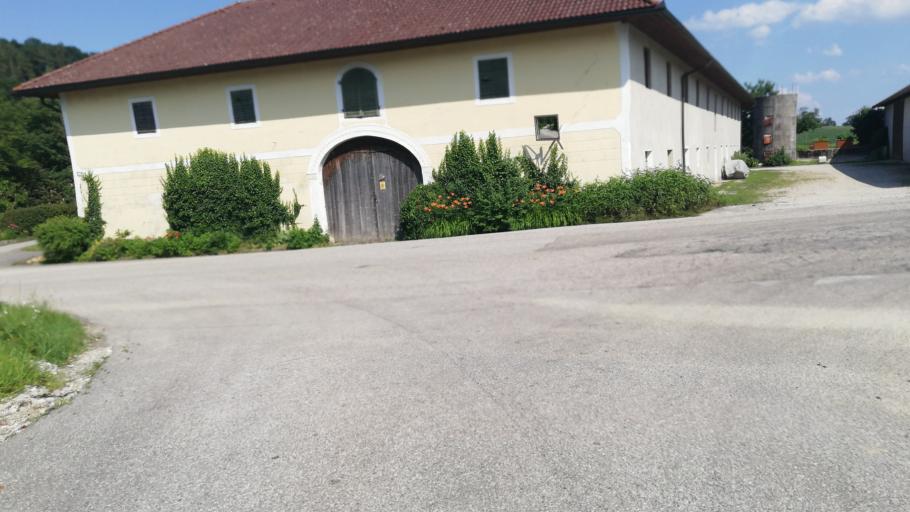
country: AT
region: Upper Austria
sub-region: Wels-Land
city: Gunskirchen
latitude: 48.1602
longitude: 13.9158
